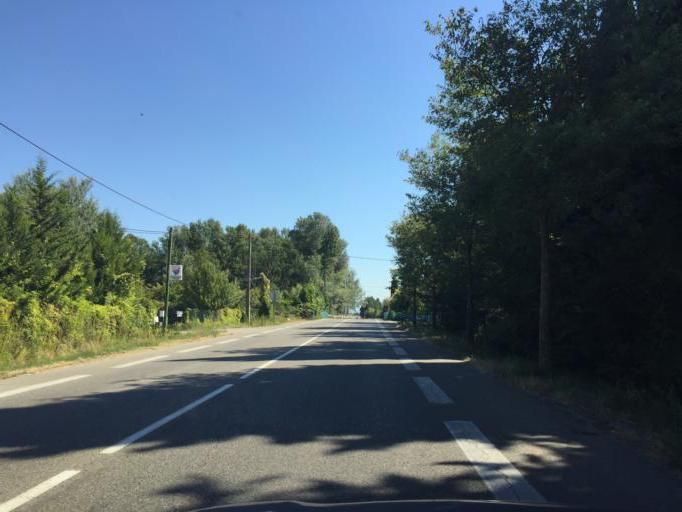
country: FR
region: Provence-Alpes-Cote d'Azur
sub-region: Departement du Vaucluse
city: Jonquerettes
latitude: 43.9619
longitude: 4.9471
